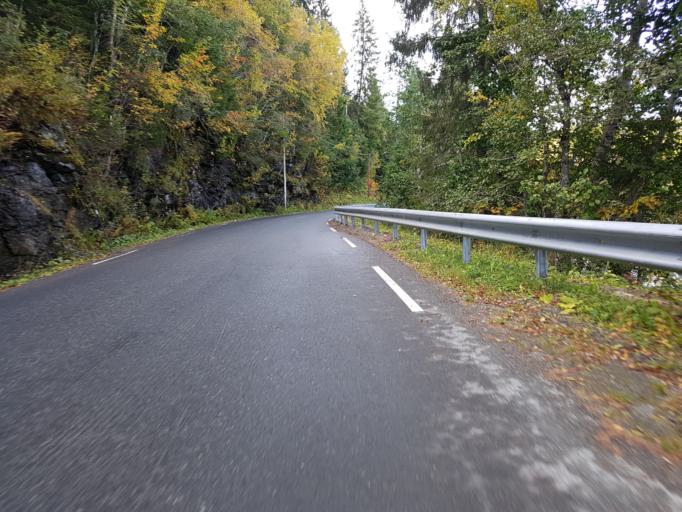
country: NO
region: Sor-Trondelag
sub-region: Klaebu
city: Klaebu
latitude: 63.3435
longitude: 10.5521
